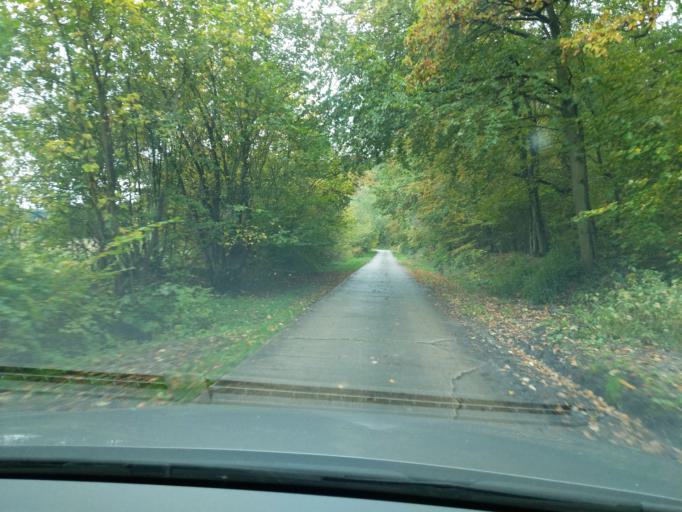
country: DE
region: Schleswig-Holstein
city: Buchhorst
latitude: 53.3948
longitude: 10.5584
